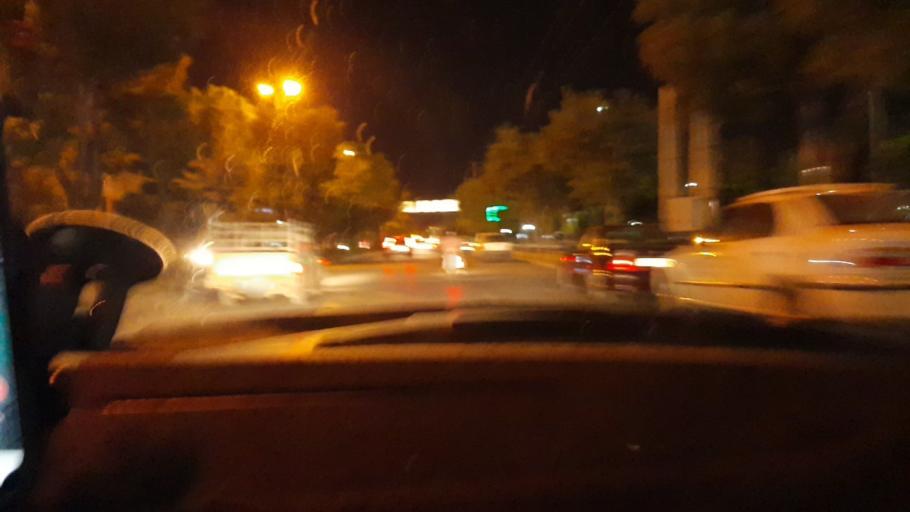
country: IR
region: Markazi
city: Arak
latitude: 34.1077
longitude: 49.6974
